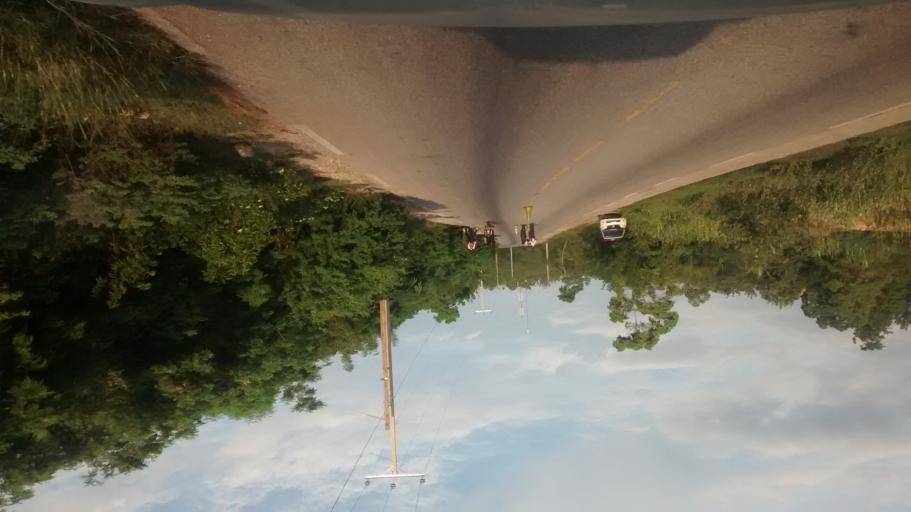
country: HT
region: Ouest
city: Grangwav
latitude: 18.4270
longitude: -72.8100
